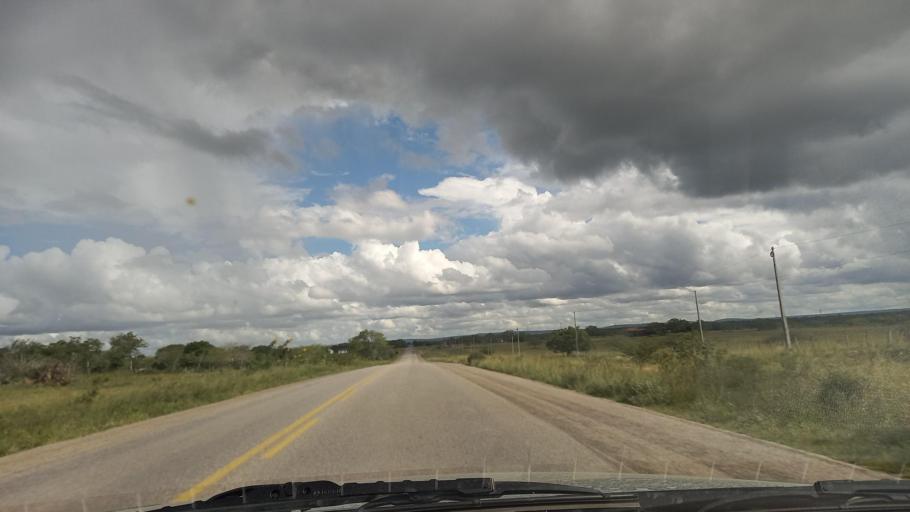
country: BR
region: Pernambuco
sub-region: Cachoeirinha
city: Cachoeirinha
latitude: -8.5234
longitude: -36.2593
